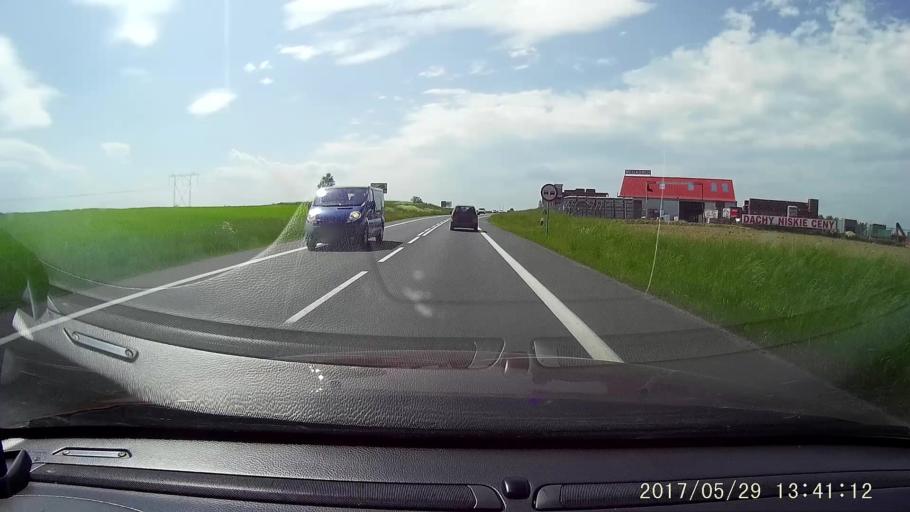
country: PL
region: Lower Silesian Voivodeship
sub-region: Powiat lubanski
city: Luban
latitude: 51.1332
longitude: 15.2598
